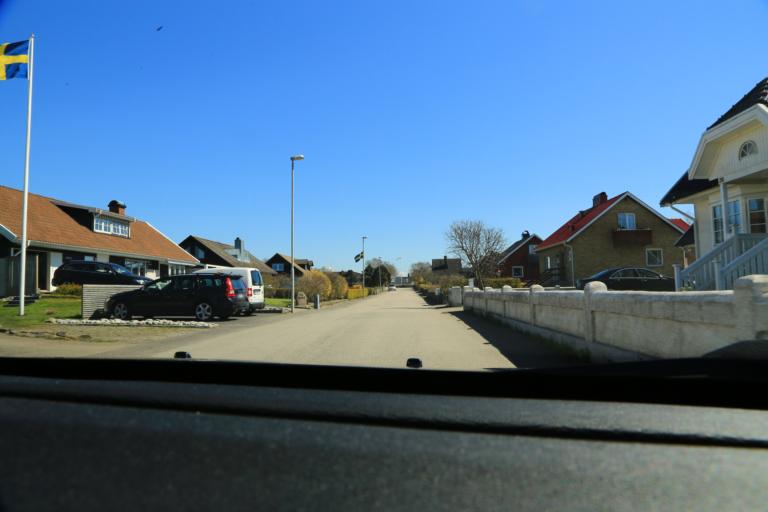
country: SE
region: Halland
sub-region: Varbergs Kommun
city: Traslovslage
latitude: 57.0546
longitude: 12.2819
